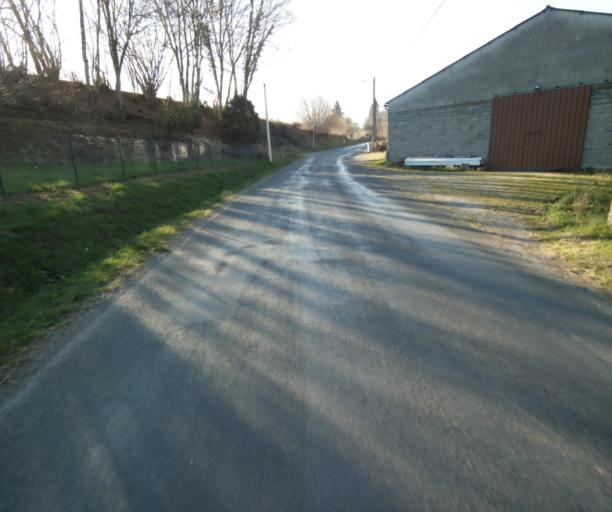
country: FR
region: Limousin
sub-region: Departement de la Correze
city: Saint-Clement
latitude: 45.3437
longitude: 1.6668
